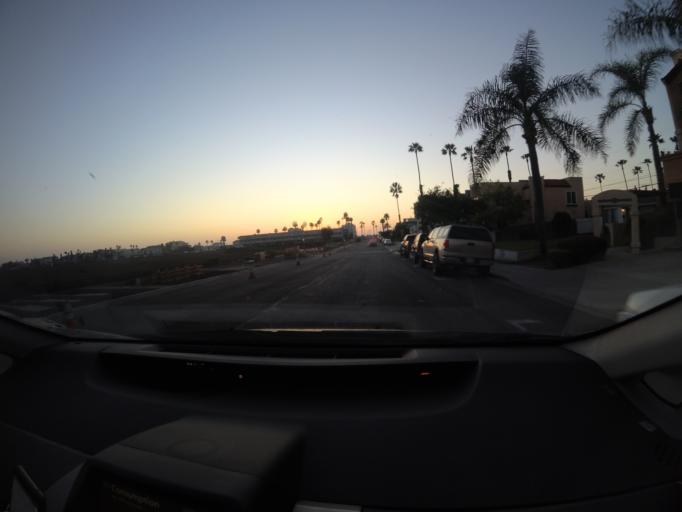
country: US
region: California
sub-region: San Diego County
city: Imperial Beach
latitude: 32.5766
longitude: -117.1289
